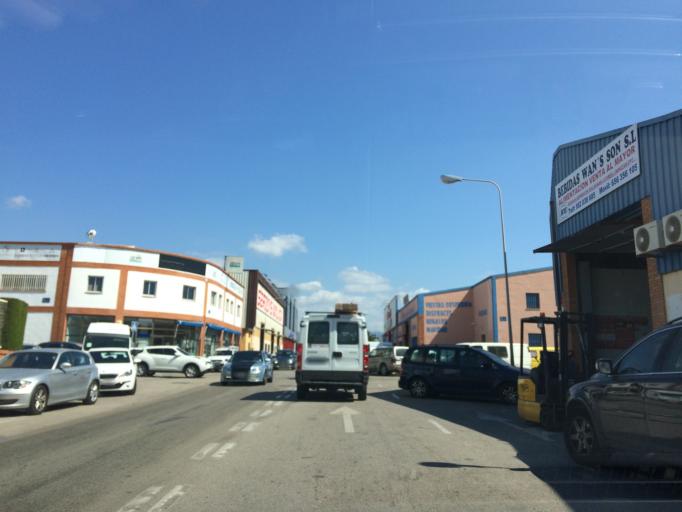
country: ES
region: Andalusia
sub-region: Provincia de Malaga
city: Malaga
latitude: 36.7058
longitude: -4.4760
